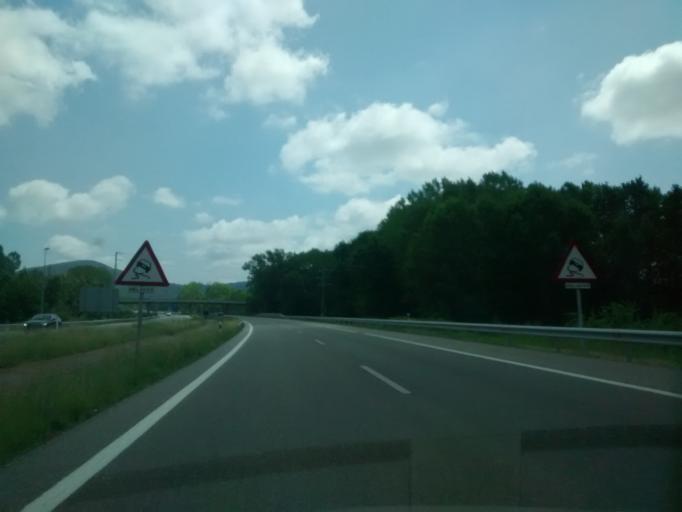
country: ES
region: Castille and Leon
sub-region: Provincia de Leon
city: Ponferrada
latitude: 42.5830
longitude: -6.6225
